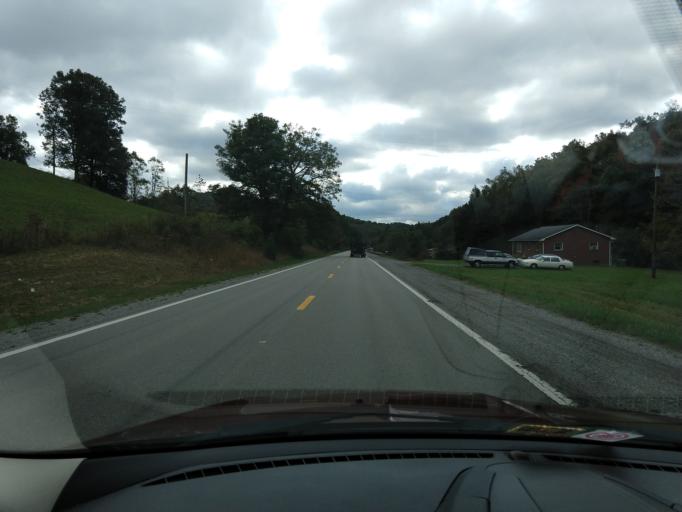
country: US
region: West Virginia
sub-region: Barbour County
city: Belington
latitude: 39.0414
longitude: -79.9557
